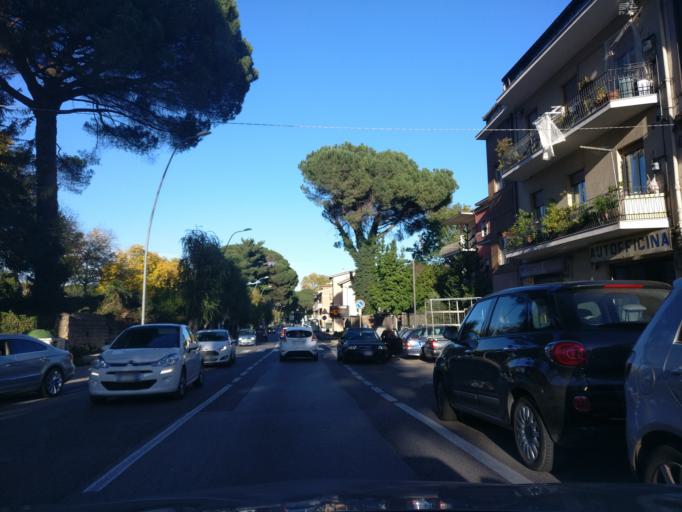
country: IT
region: Campania
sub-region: Provincia di Avellino
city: Torelli-Torrette
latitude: 40.9093
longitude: 14.7680
